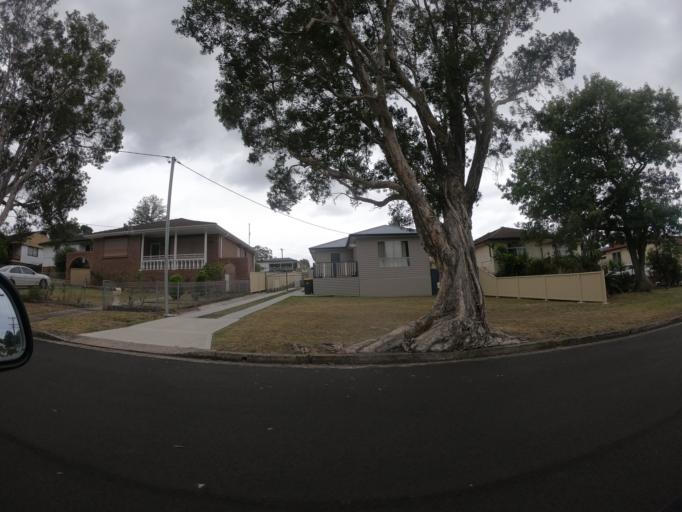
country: AU
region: New South Wales
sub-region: Wollongong
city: Berkeley
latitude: -34.4805
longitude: 150.8412
